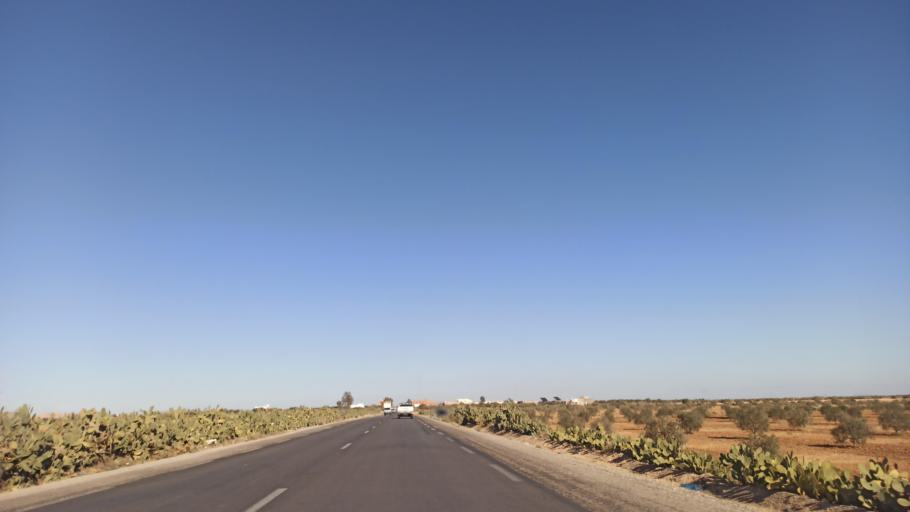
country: TN
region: Sidi Bu Zayd
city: Bi'r al Hufayy
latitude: 34.9651
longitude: 9.2248
